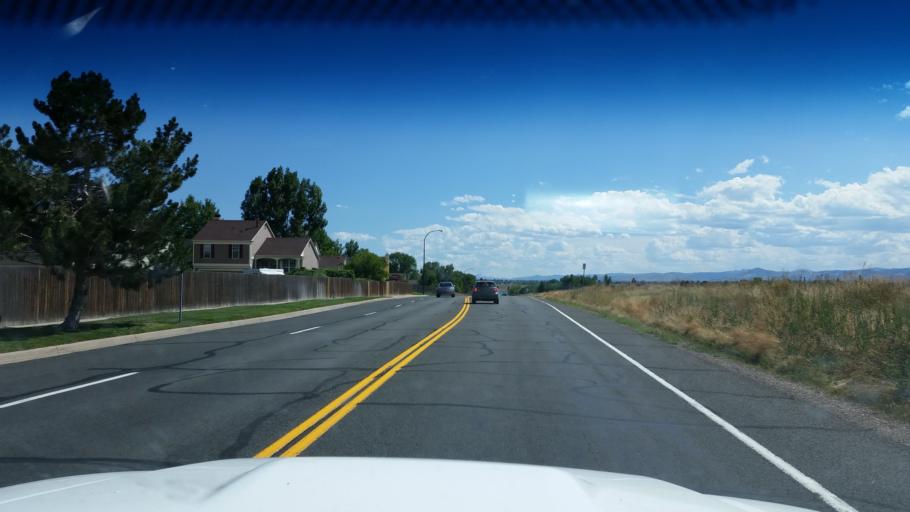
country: US
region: Colorado
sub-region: Broomfield County
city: Broomfield
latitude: 39.8834
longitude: -105.1288
